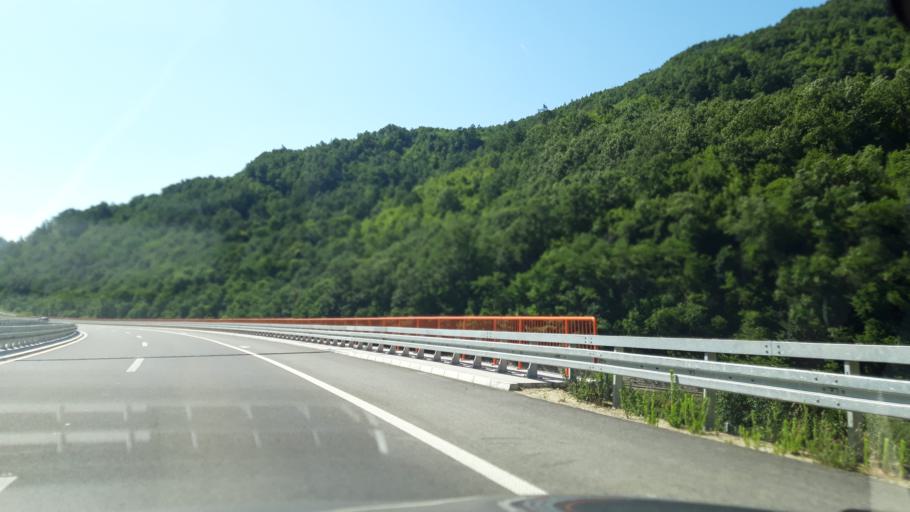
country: RS
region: Central Serbia
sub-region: Jablanicki Okrug
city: Vlasotince
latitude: 42.8719
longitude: 22.0999
